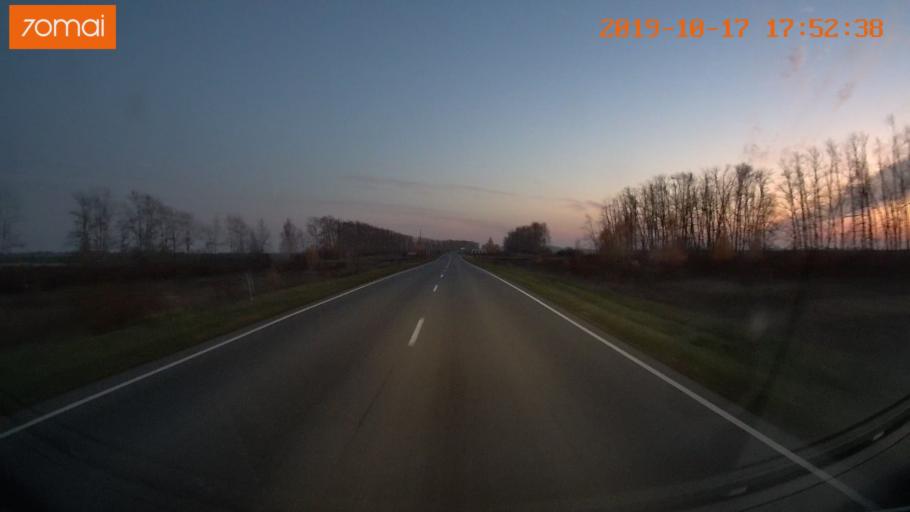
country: RU
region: Tula
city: Kurkino
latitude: 53.6318
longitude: 38.6826
